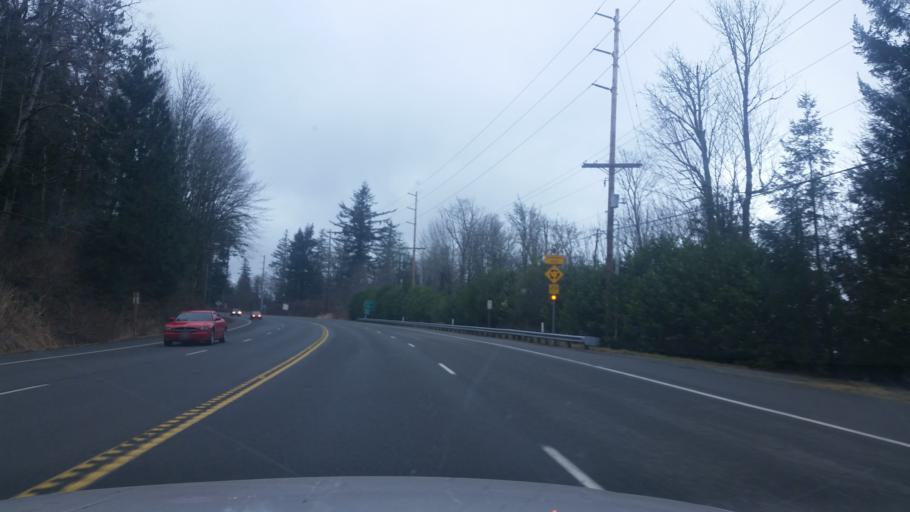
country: US
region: Washington
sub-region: King County
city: Snoqualmie
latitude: 47.5163
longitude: -121.8363
